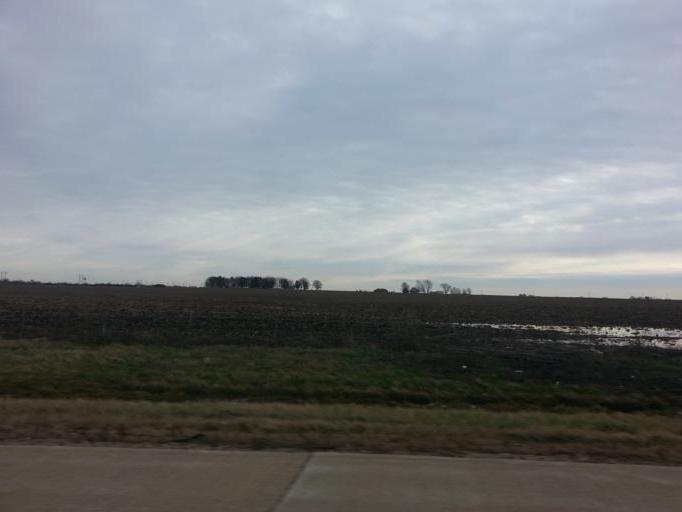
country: US
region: Illinois
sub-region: Woodford County
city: El Paso
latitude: 40.7260
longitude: -89.0341
